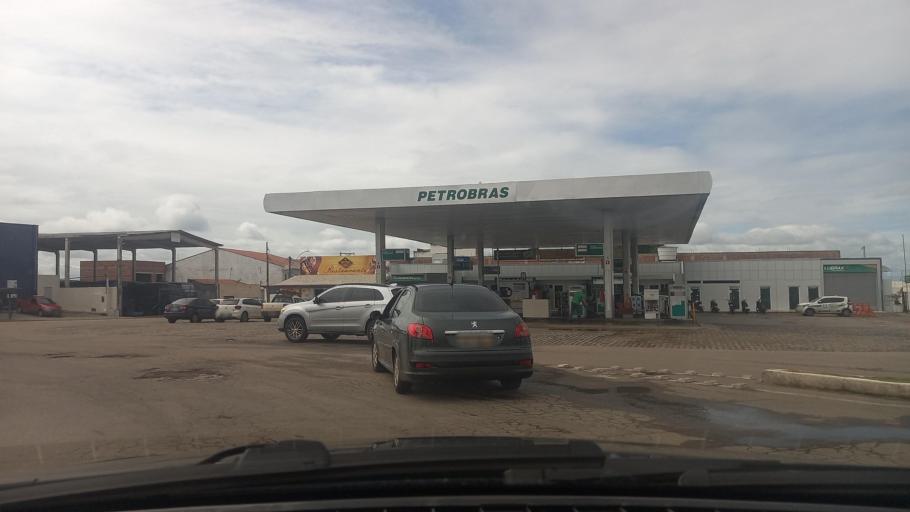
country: BR
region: Bahia
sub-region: Paulo Afonso
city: Paulo Afonso
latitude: -9.4467
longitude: -38.2214
